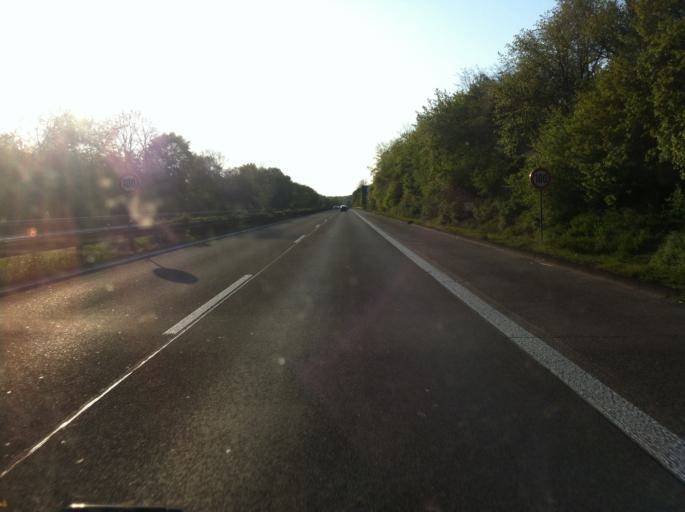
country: DE
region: North Rhine-Westphalia
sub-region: Regierungsbezirk Koln
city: Ostheim
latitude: 50.9098
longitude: 7.0409
